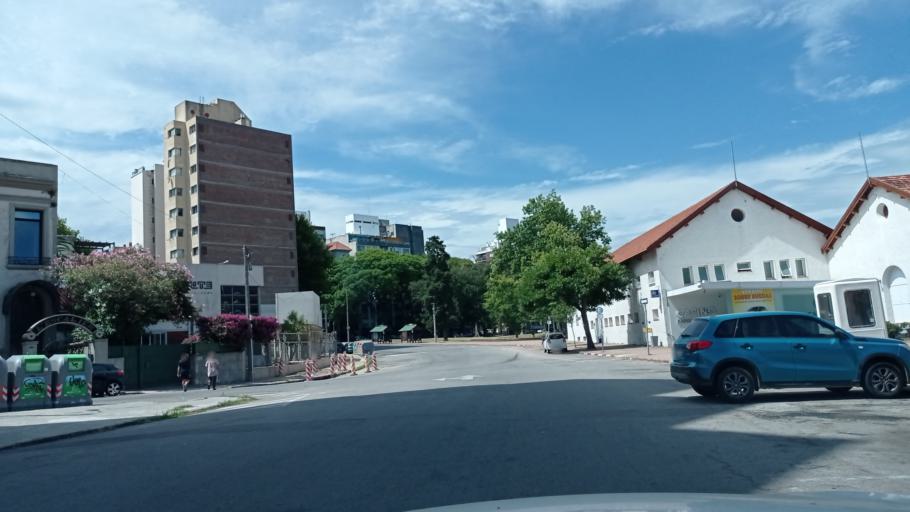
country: UY
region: Montevideo
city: Montevideo
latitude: -34.9128
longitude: -56.1698
